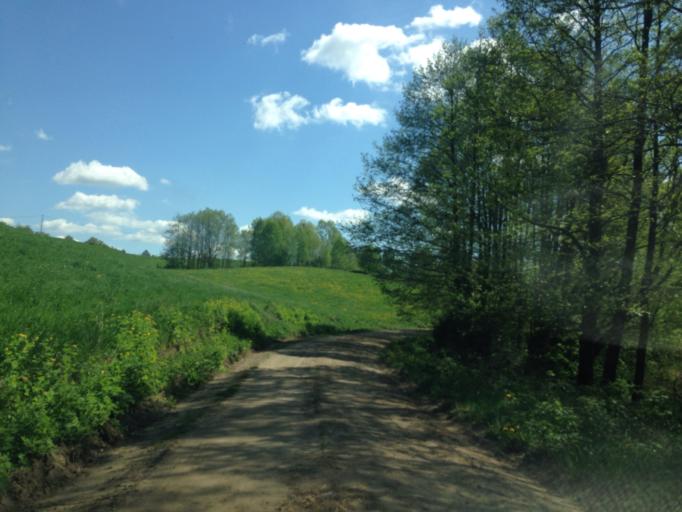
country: PL
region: Kujawsko-Pomorskie
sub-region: Powiat brodnicki
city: Brzozie
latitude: 53.3062
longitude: 19.6460
